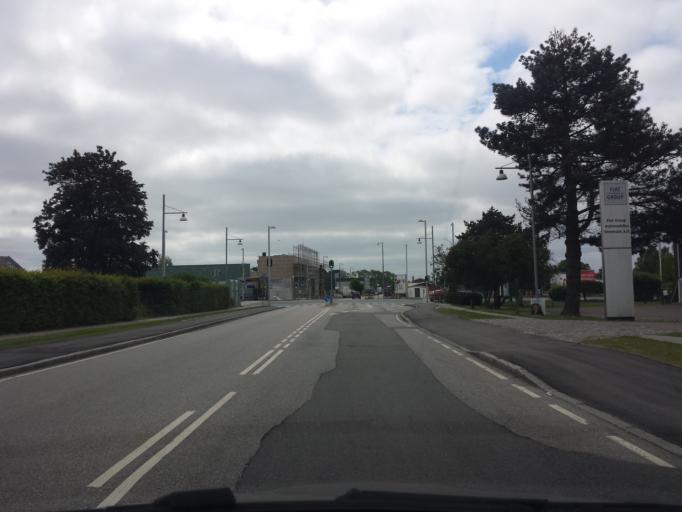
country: DK
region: Capital Region
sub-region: Albertslund Kommune
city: Albertslund
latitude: 55.6648
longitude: 12.3726
